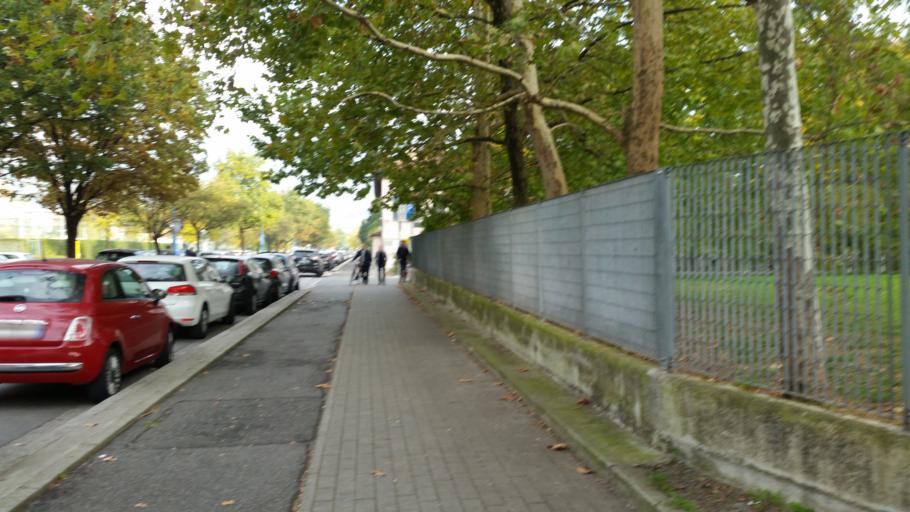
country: IT
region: Lombardy
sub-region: Provincia di Brescia
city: Collebeato
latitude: 45.5637
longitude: 10.2319
